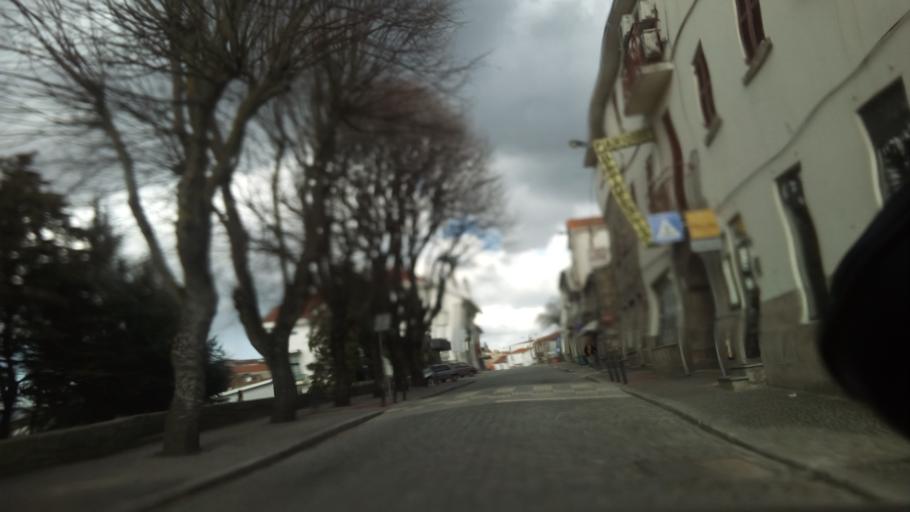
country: PT
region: Guarda
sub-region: Celorico da Beira
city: Celorico da Beira
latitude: 40.6341
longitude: -7.3945
